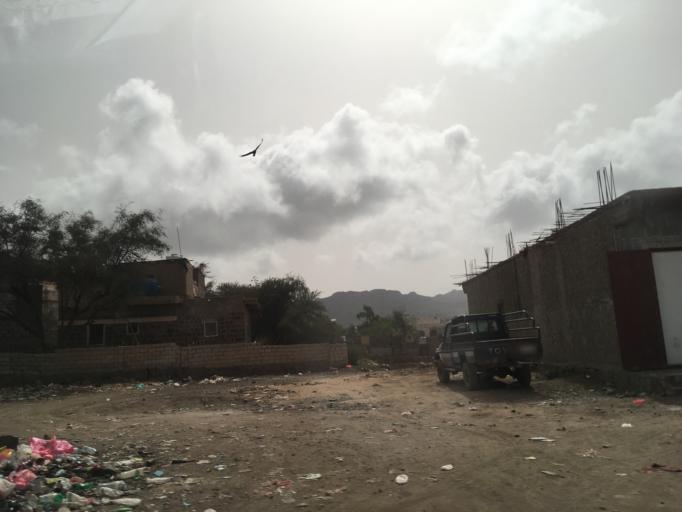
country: YE
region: Ad Dali'
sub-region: Ad Dhale'e
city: Dhalie
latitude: 13.7033
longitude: 44.7377
